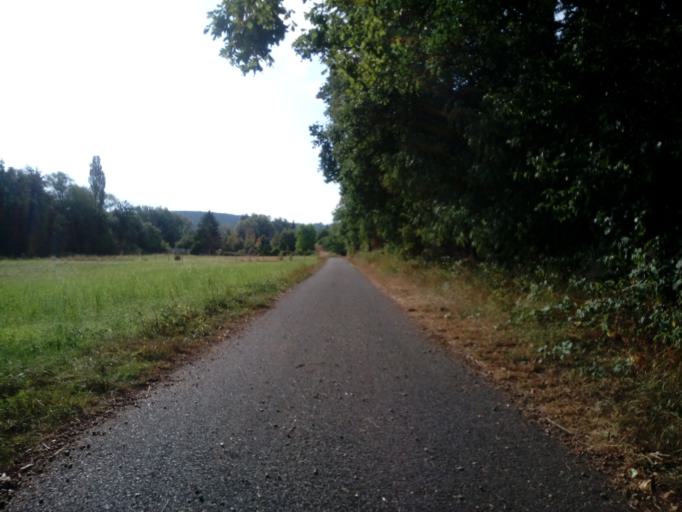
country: DE
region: Rheinland-Pfalz
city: Roxheim
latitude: 49.8687
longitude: 7.8155
